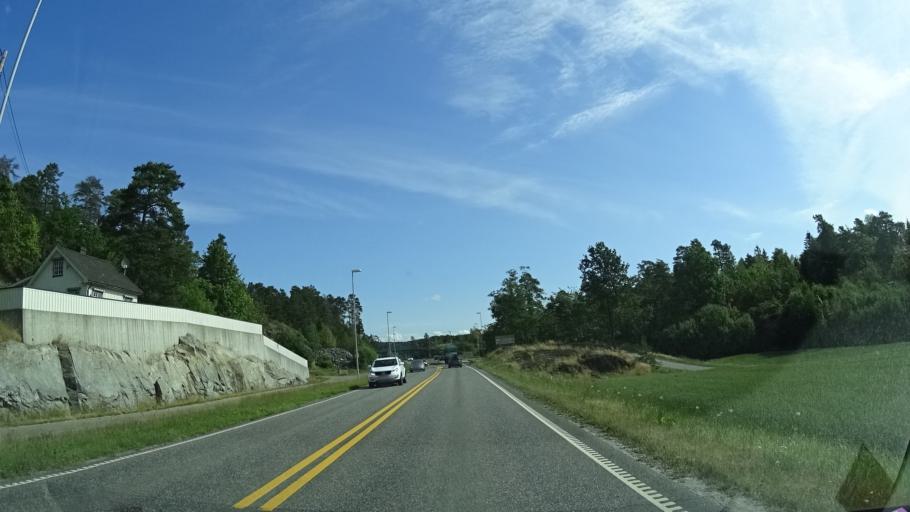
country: NO
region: Telemark
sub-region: Bamble
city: Langesund
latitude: 59.0132
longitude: 9.6704
